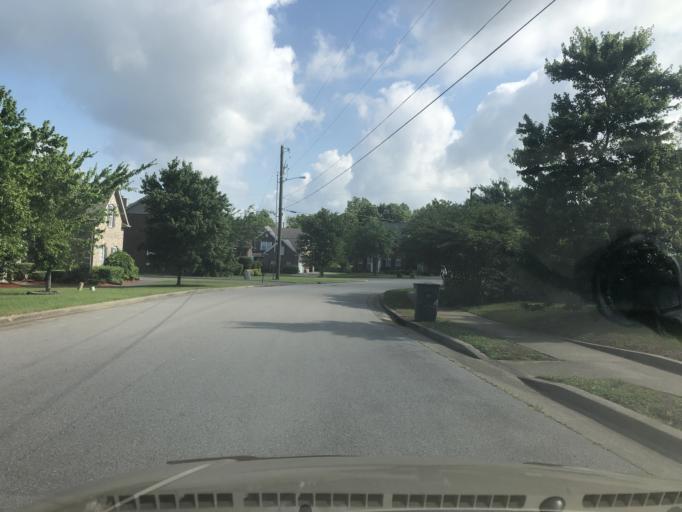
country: US
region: Tennessee
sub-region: Wilson County
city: Green Hill
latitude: 36.2277
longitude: -86.5930
